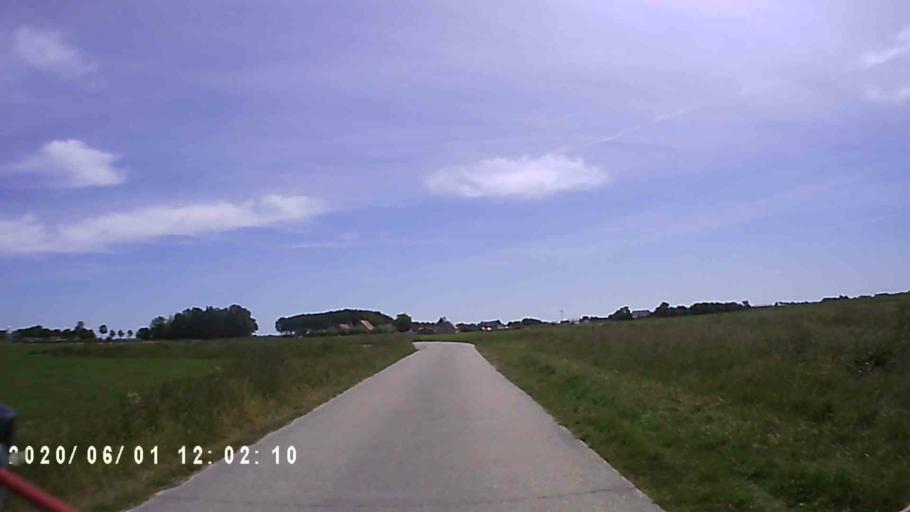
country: NL
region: Friesland
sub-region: Gemeente Harlingen
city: Harlingen
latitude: 53.1587
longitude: 5.4573
